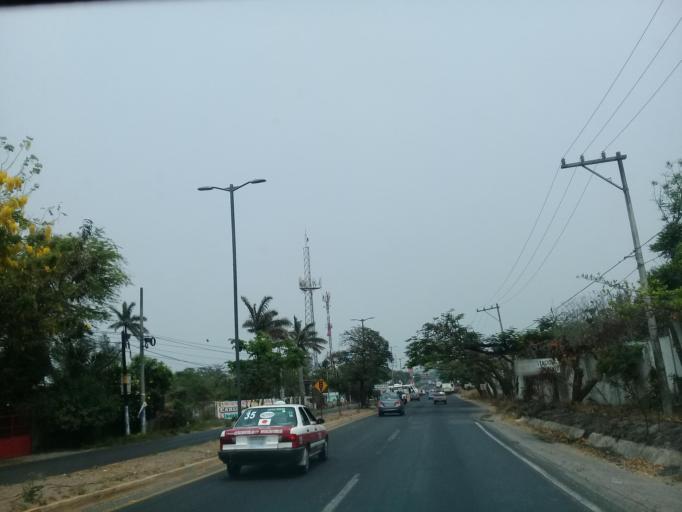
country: MX
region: Veracruz
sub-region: Veracruz
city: Las Amapolas
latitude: 19.1521
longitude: -96.1800
